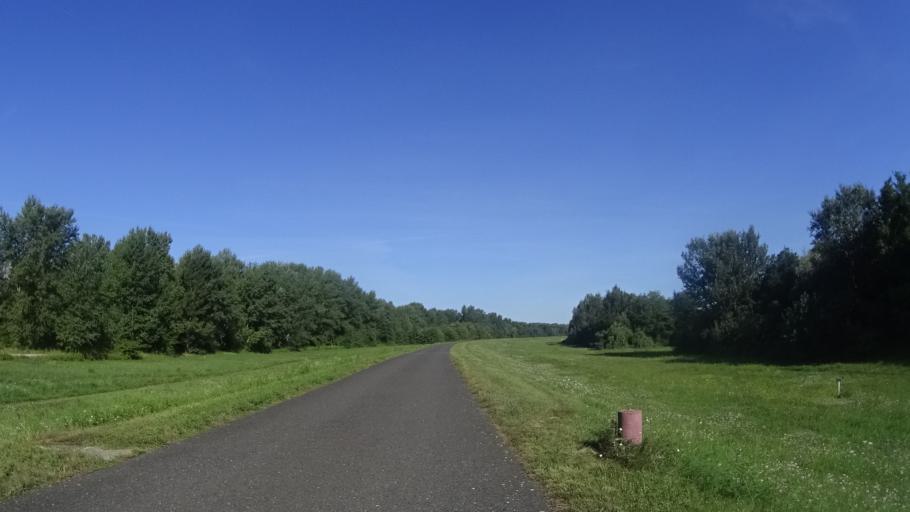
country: HU
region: Gyor-Moson-Sopron
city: Rajka
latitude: 48.0652
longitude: 17.1755
